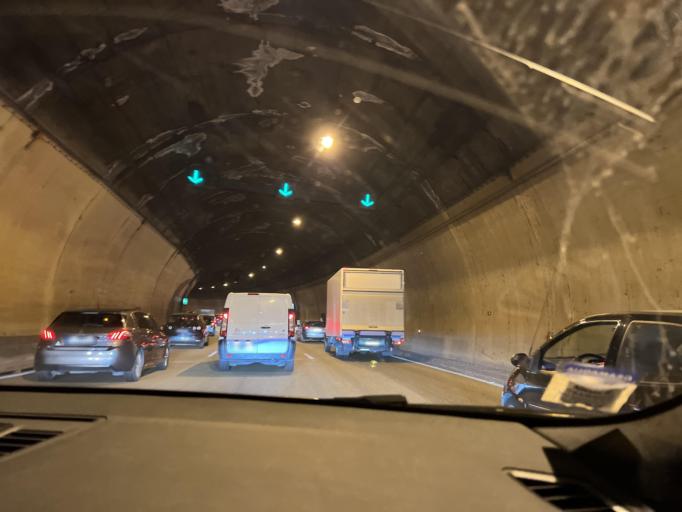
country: FR
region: Provence-Alpes-Cote d'Azur
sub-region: Departement des Alpes-Maritimes
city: Falicon
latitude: 43.7347
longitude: 7.2527
